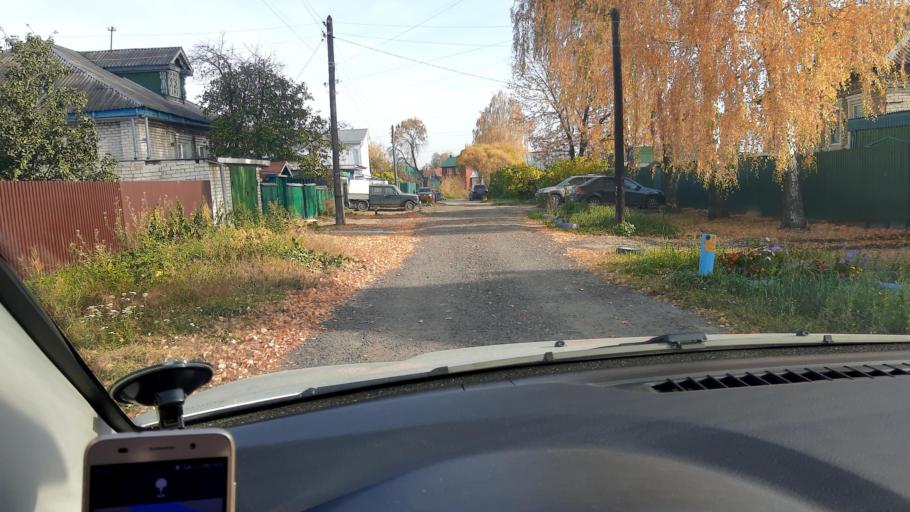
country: RU
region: Nizjnij Novgorod
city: Nizhniy Novgorod
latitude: 56.2828
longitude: 43.8999
